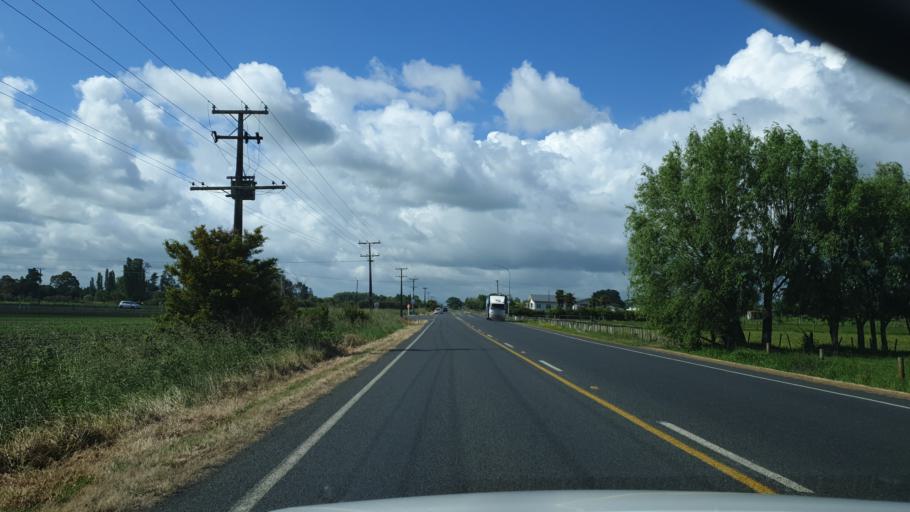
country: NZ
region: Waikato
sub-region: Hauraki District
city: Paeroa
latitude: -37.5134
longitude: 175.4969
